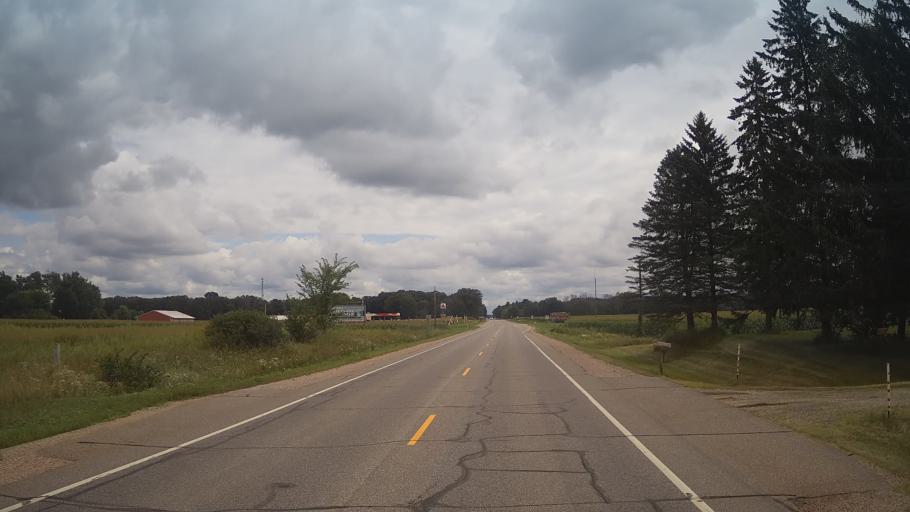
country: US
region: Wisconsin
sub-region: Adams County
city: Friendship
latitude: 44.0394
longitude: -89.9413
